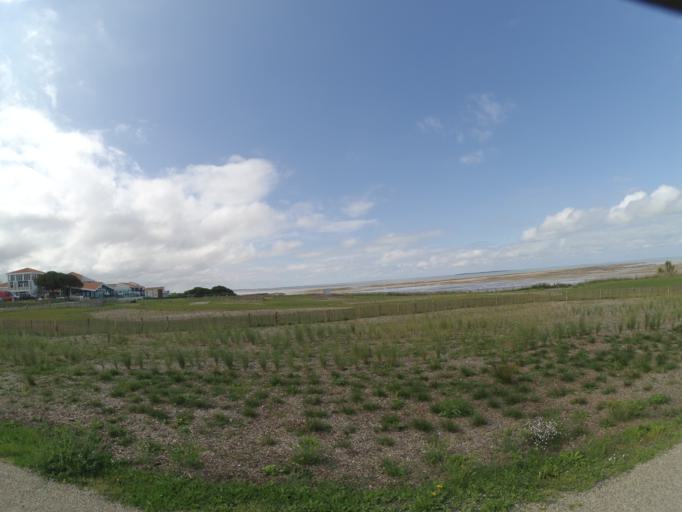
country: FR
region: Poitou-Charentes
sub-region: Departement de la Charente-Maritime
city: Chatelaillon-Plage
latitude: 46.0590
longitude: -1.0887
